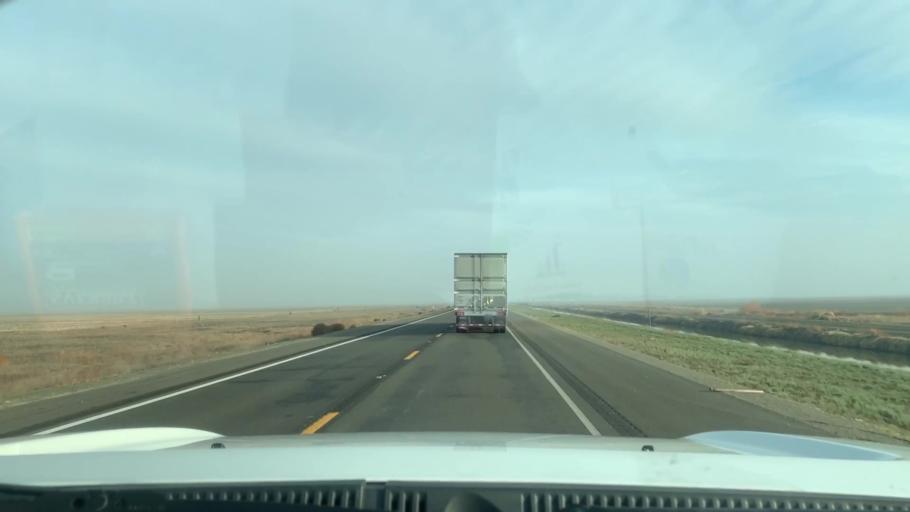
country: US
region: California
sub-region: Kings County
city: Kettleman City
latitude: 36.1001
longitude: -119.9067
